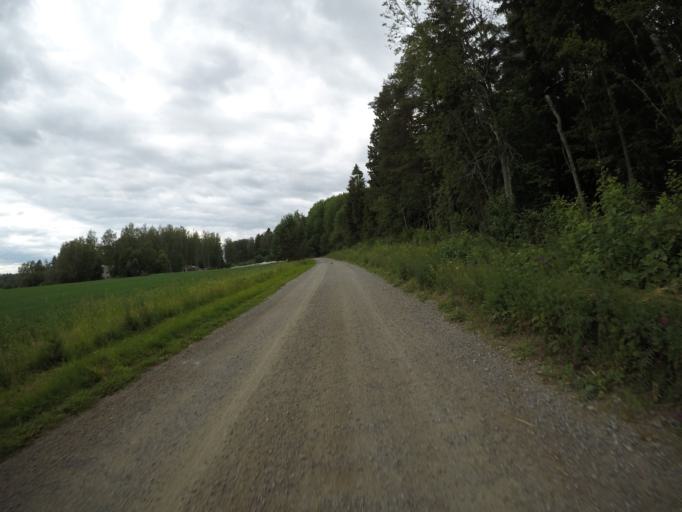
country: FI
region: Haeme
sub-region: Haemeenlinna
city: Haemeenlinna
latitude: 60.9765
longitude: 24.4559
